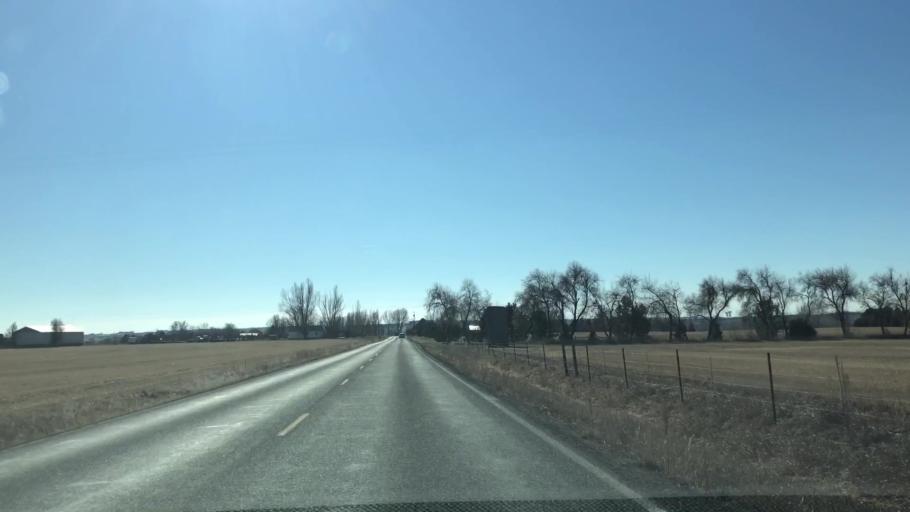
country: US
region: Colorado
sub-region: Weld County
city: Windsor
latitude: 40.4949
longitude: -104.9442
